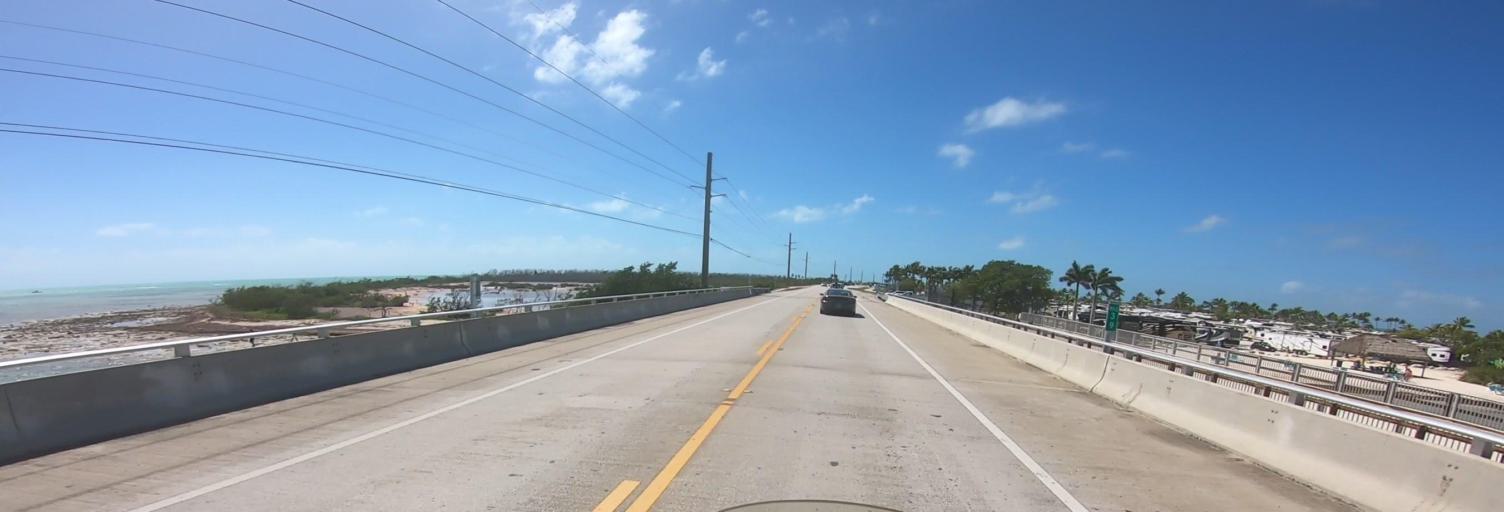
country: US
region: Florida
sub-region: Monroe County
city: Big Pine Key
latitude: 24.6738
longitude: -81.2432
